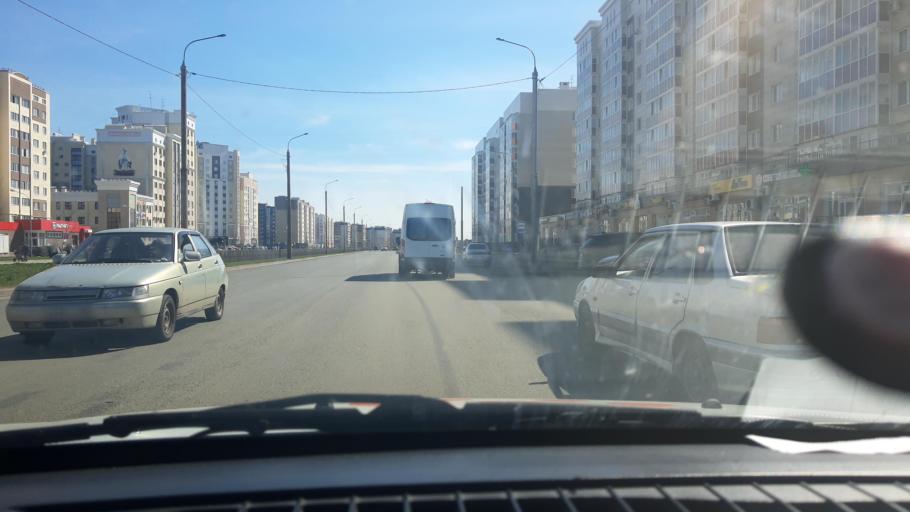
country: RU
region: Bashkortostan
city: Sterlitamak
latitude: 53.6288
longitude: 55.8959
